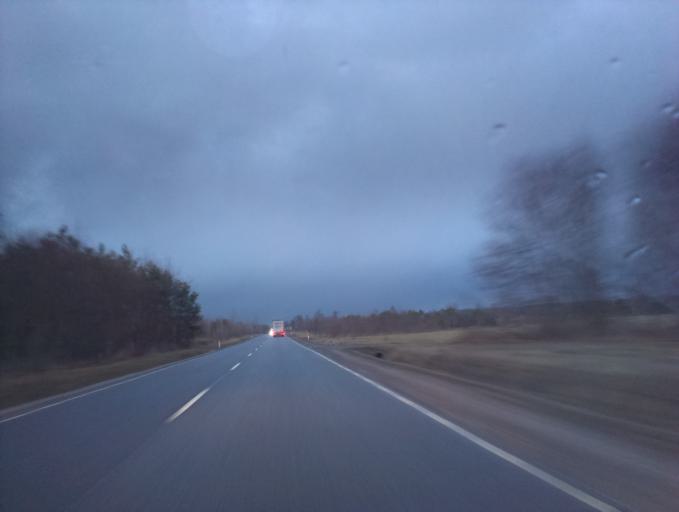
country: PL
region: Lodz Voivodeship
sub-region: Powiat opoczynski
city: Zarnow
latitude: 51.2353
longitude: 20.1772
